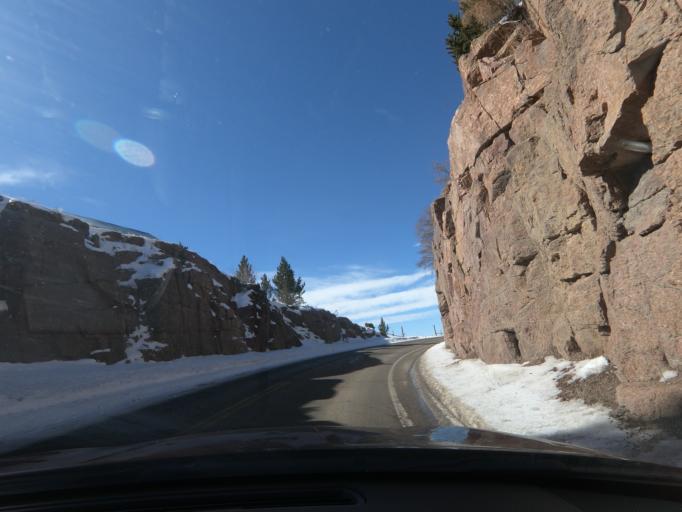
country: US
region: Colorado
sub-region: Teller County
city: Cripple Creek
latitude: 38.7101
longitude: -105.1456
